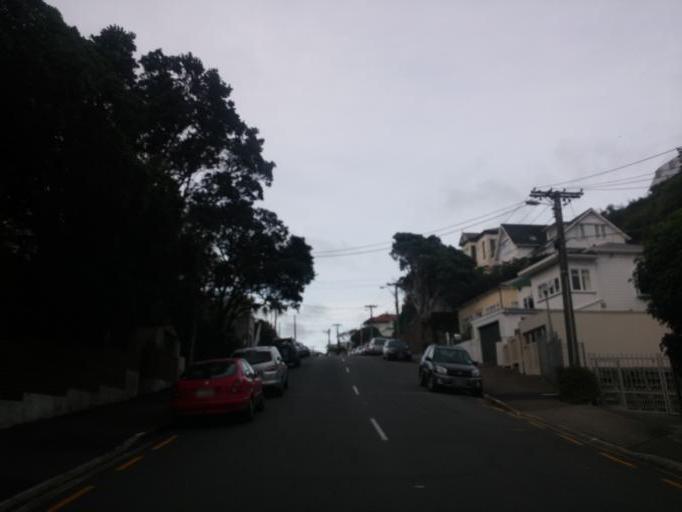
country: NZ
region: Wellington
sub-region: Wellington City
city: Wellington
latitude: -41.3032
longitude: 174.7670
